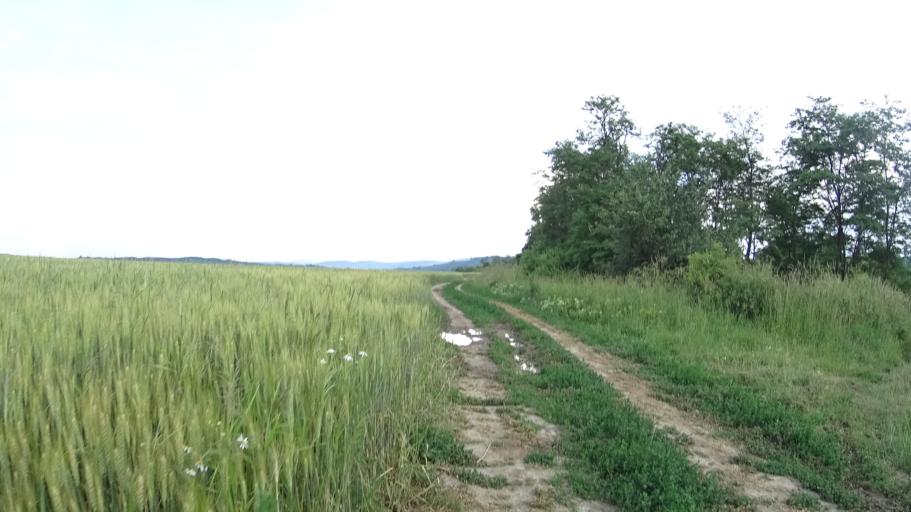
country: HU
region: Nograd
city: Retsag
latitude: 47.9273
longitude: 19.1518
